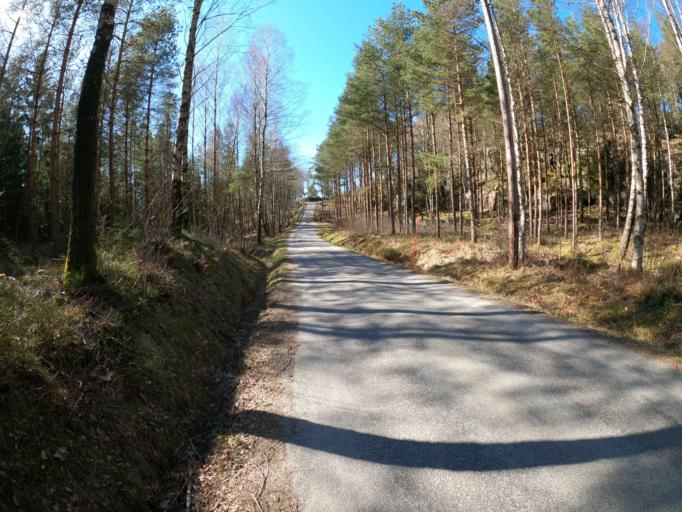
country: SE
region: Vaestra Goetaland
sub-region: Harryda Kommun
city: Molnlycke
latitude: 57.6338
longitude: 12.1181
